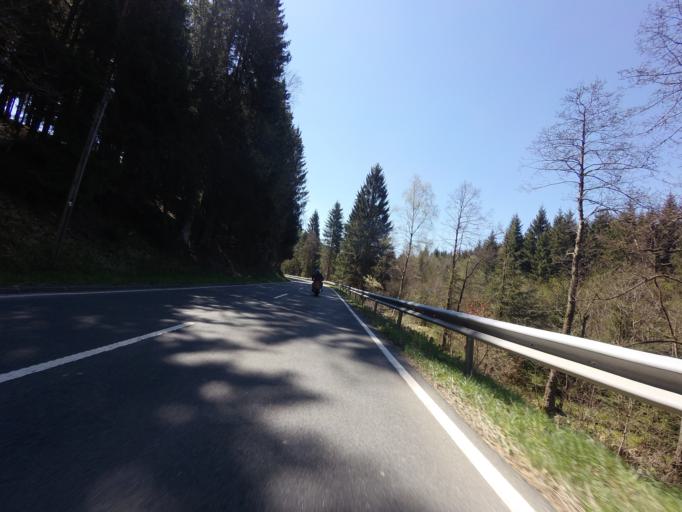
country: DE
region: North Rhine-Westphalia
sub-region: Regierungsbezirk Arnsberg
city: Erndtebruck
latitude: 51.0504
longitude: 8.2304
